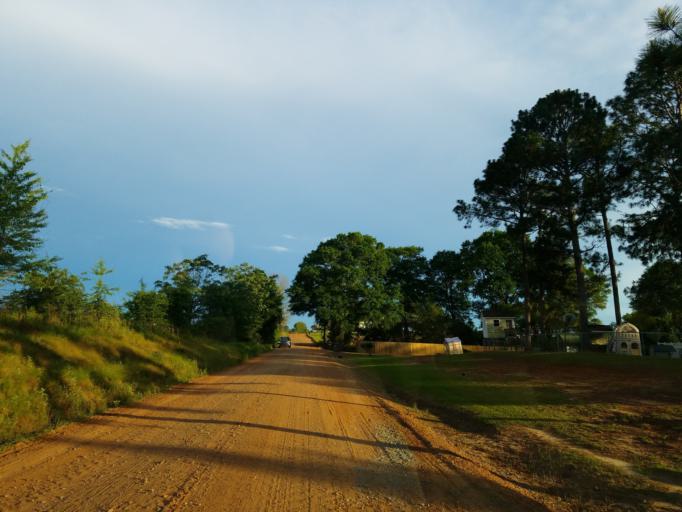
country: US
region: Georgia
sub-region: Turner County
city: Ashburn
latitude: 31.6457
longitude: -83.6208
